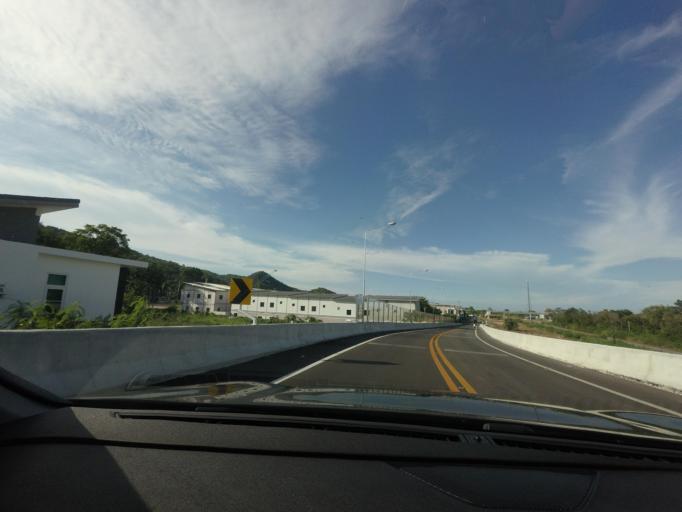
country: TH
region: Prachuap Khiri Khan
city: Pran Buri
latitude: 12.4440
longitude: 99.9606
